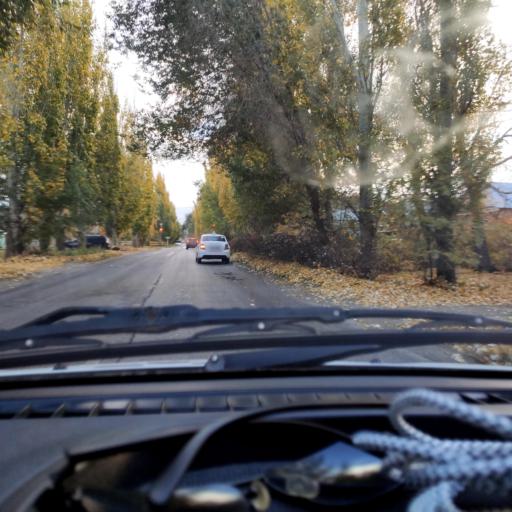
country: RU
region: Samara
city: Tol'yatti
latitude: 53.5347
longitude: 49.4175
